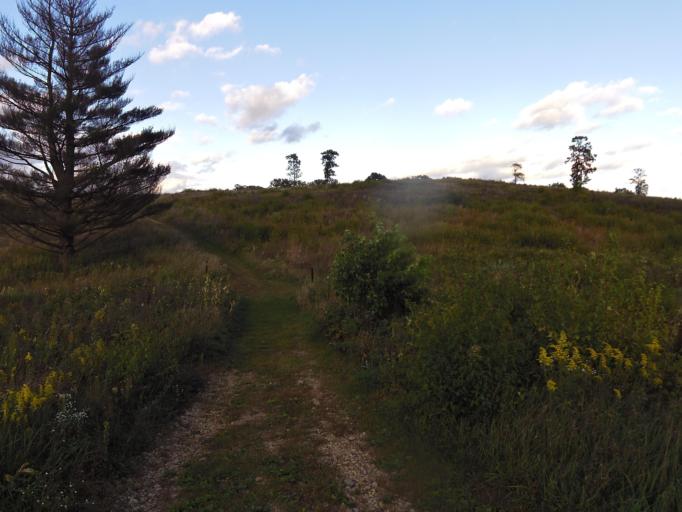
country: US
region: Minnesota
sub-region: Washington County
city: Lake Saint Croix Beach
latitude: 44.9367
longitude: -92.7858
